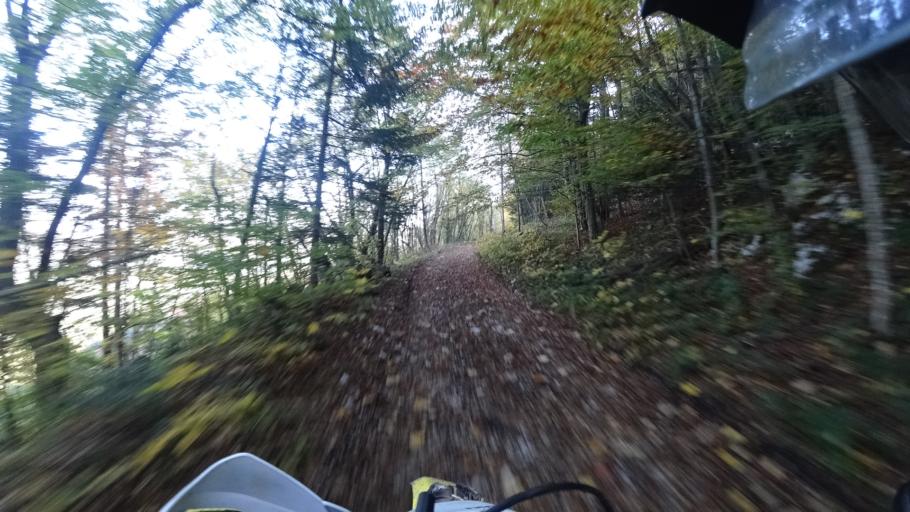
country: HR
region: Karlovacka
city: Plaski
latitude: 44.9701
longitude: 15.4348
